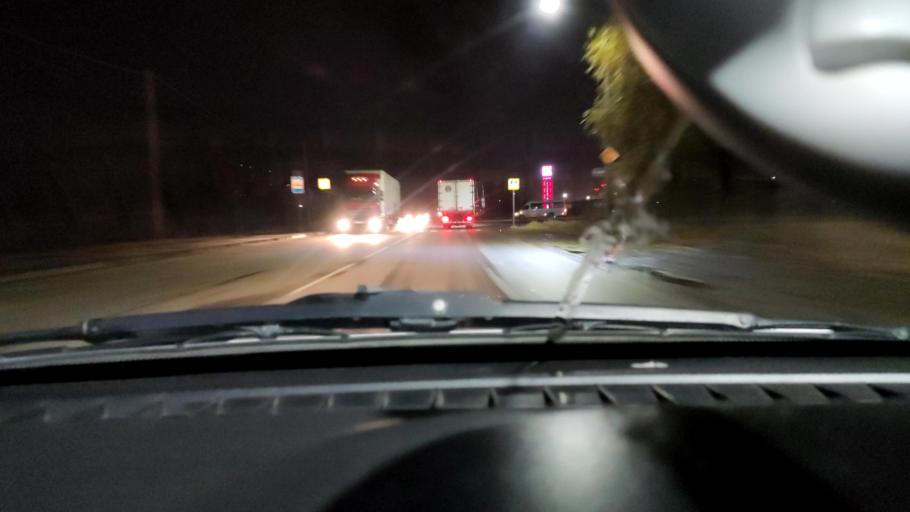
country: RU
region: Perm
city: Kondratovo
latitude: 57.9328
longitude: 56.1249
